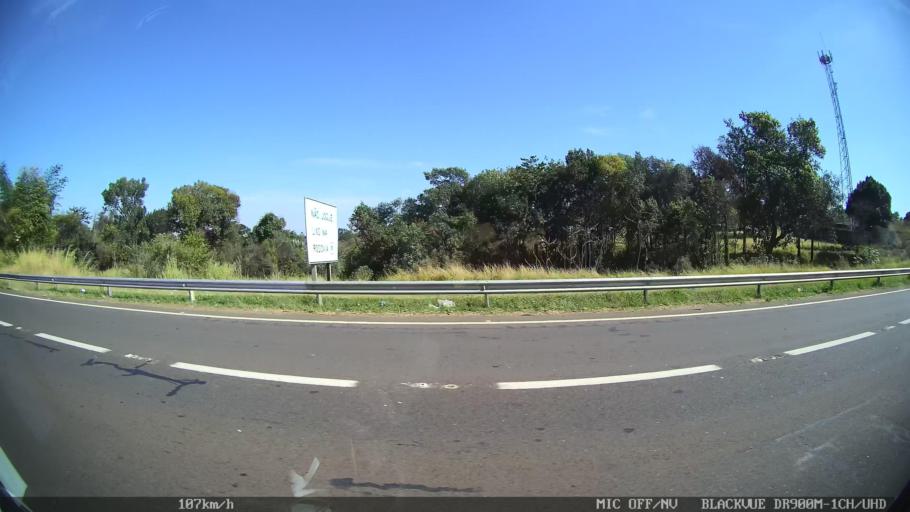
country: BR
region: Sao Paulo
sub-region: Franca
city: Franca
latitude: -20.4811
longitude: -47.4106
